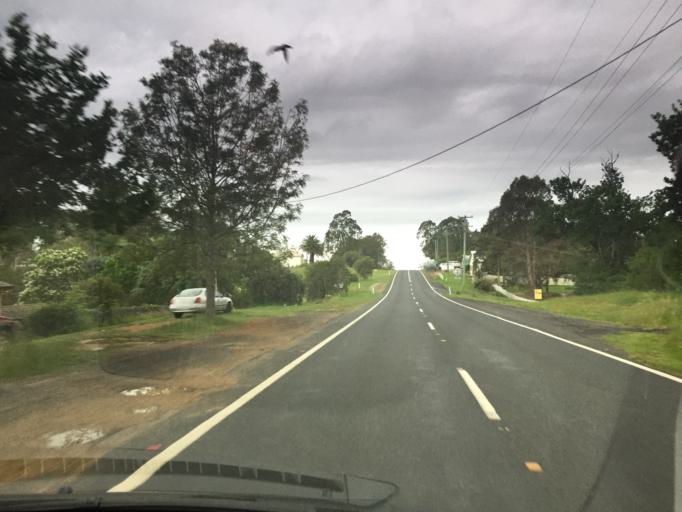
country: AU
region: New South Wales
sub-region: Bega Valley
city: Bega
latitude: -36.6300
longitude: 149.5731
